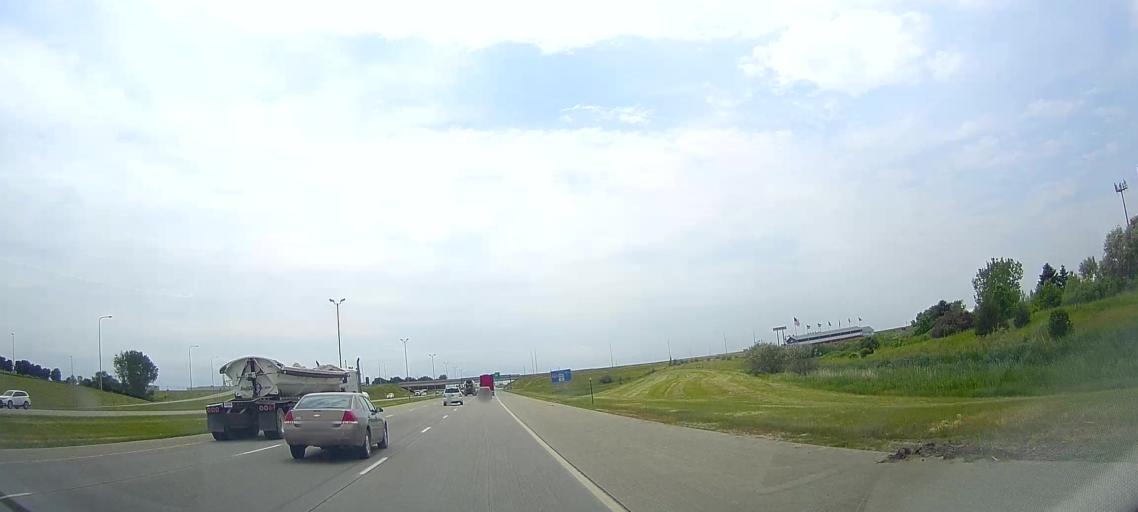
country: US
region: South Dakota
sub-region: Minnehaha County
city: Crooks
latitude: 43.6054
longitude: -96.7712
